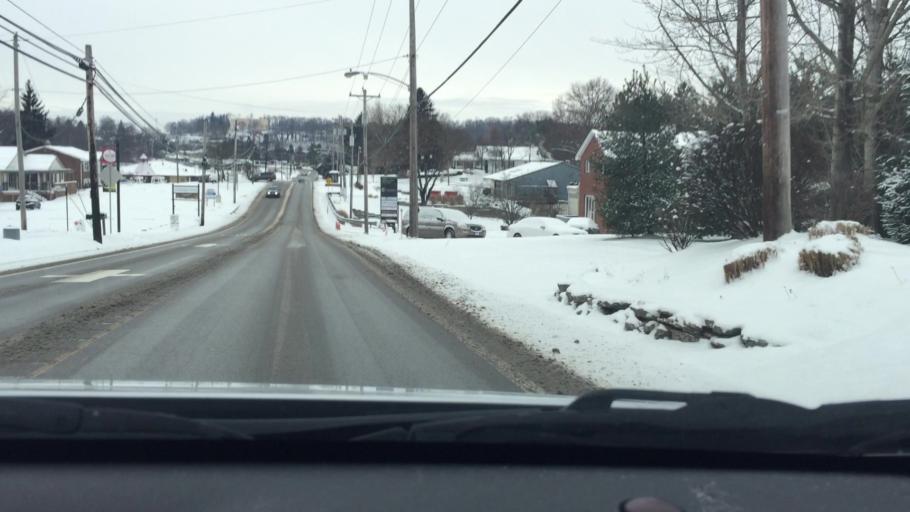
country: US
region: Pennsylvania
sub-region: Allegheny County
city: Carnot-Moon
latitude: 40.5242
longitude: -80.2244
